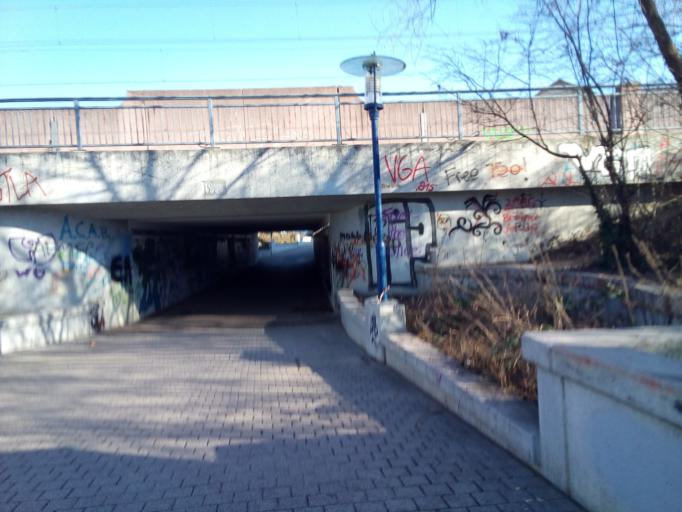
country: DE
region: Baden-Wuerttemberg
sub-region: Karlsruhe Region
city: Buhl
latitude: 48.7026
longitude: 8.1325
